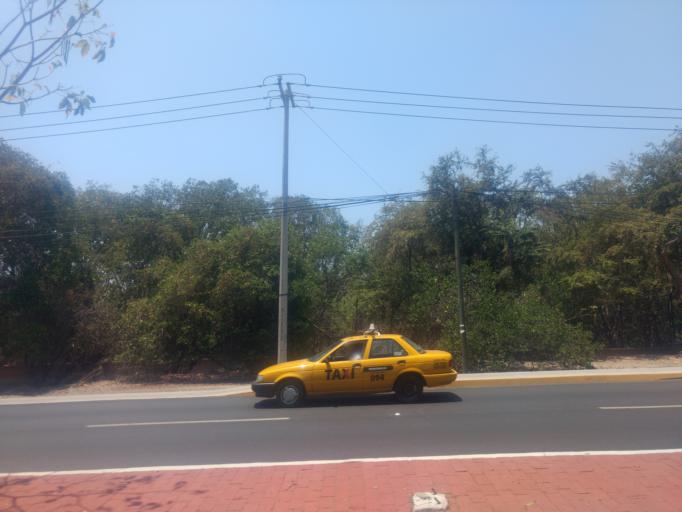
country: MX
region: Colima
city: Tapeixtles
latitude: 19.0857
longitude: -104.3054
